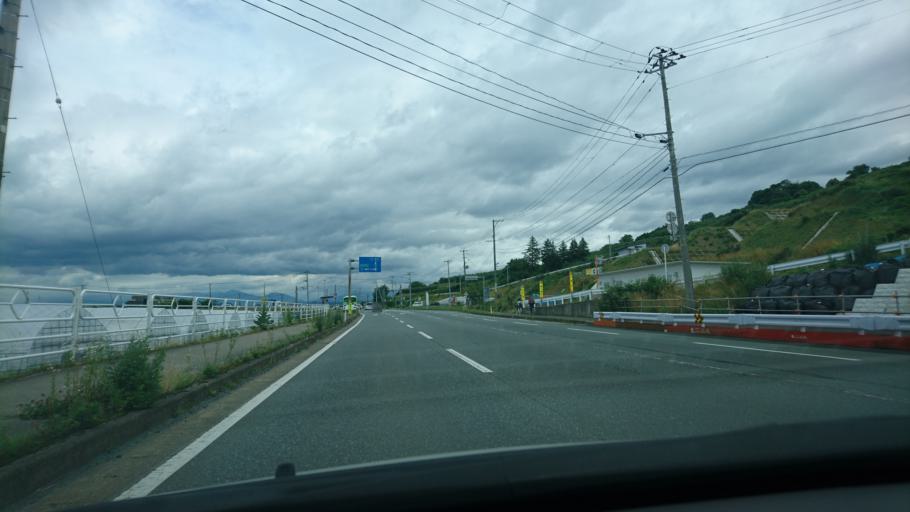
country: JP
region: Iwate
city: Morioka-shi
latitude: 39.6599
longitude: 141.1787
